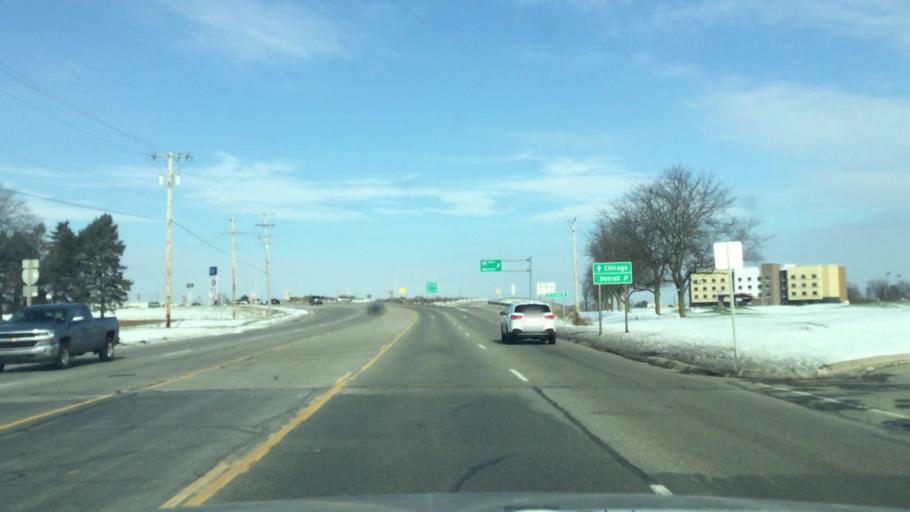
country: US
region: Michigan
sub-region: Kalamazoo County
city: Eastwood
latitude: 42.2556
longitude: -85.5308
